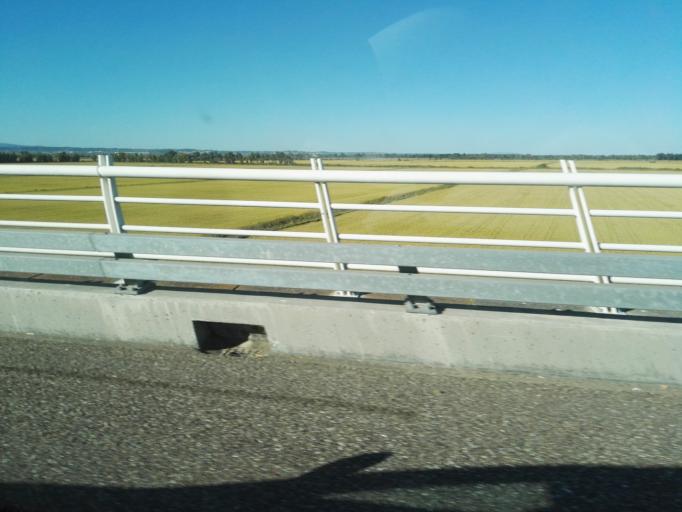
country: PT
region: Santarem
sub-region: Benavente
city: Samora Correia
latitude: 38.9668
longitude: -8.8614
